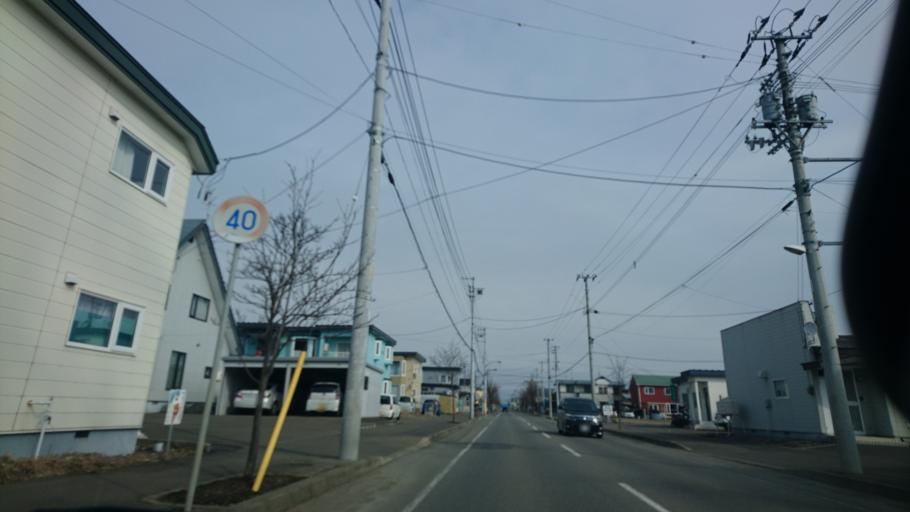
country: JP
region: Hokkaido
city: Otofuke
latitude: 42.9645
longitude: 143.2134
